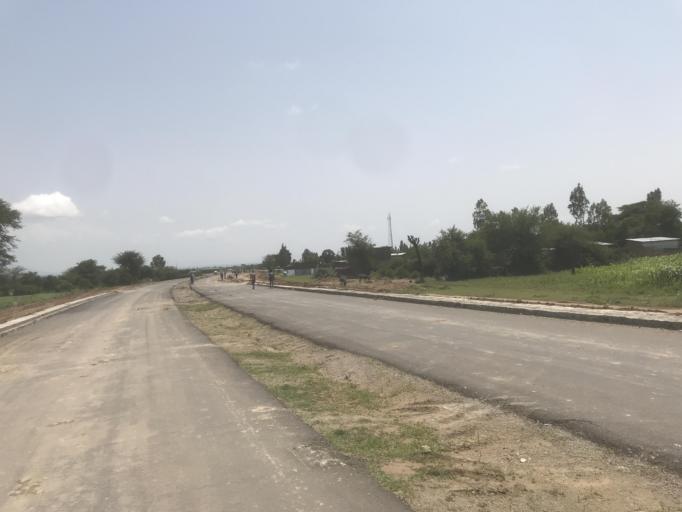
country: ET
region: Oromiya
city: Mojo
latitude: 8.2960
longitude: 38.9398
